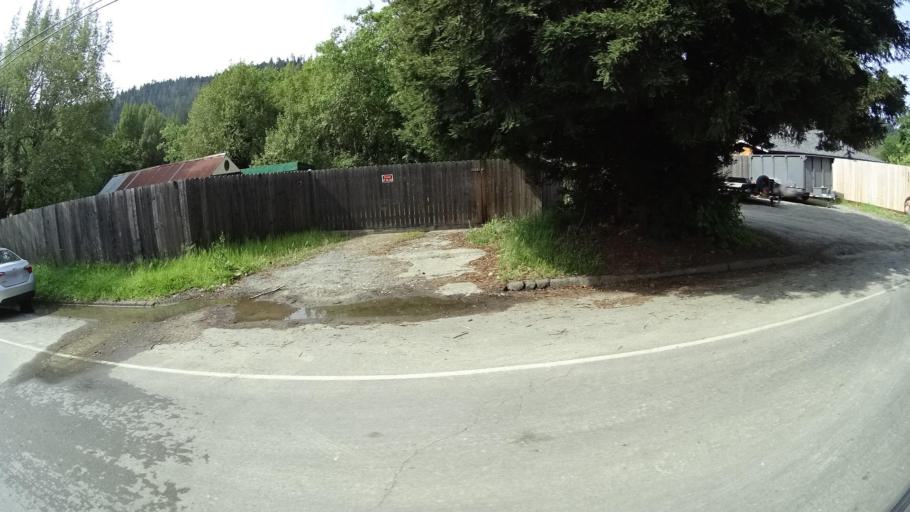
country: US
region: California
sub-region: Humboldt County
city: Redway
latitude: 40.1171
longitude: -123.8274
